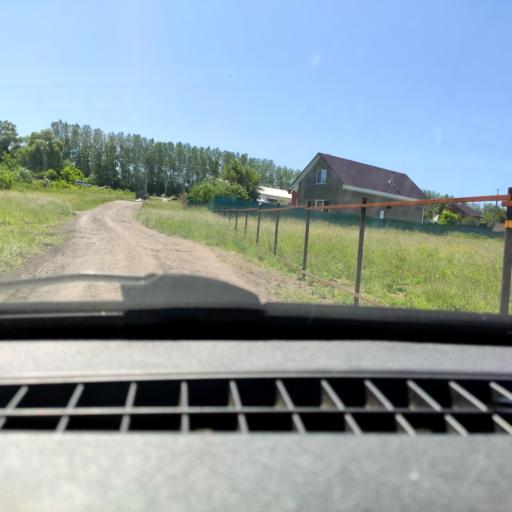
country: RU
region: Bashkortostan
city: Iglino
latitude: 54.7941
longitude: 56.2806
